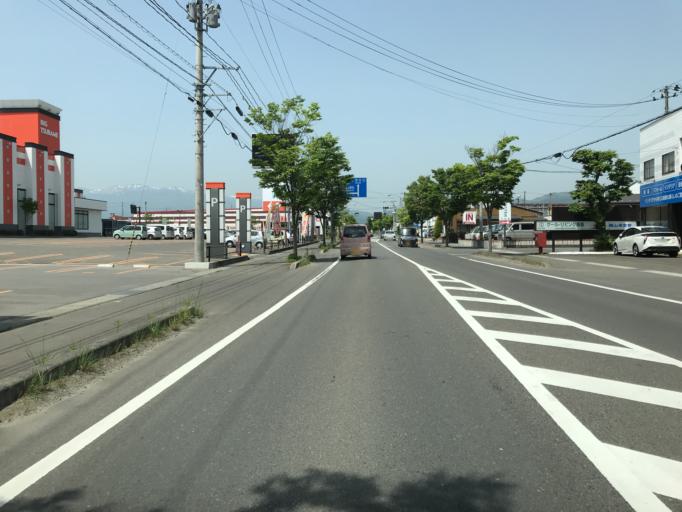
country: JP
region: Fukushima
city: Fukushima-shi
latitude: 37.7936
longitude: 140.4564
